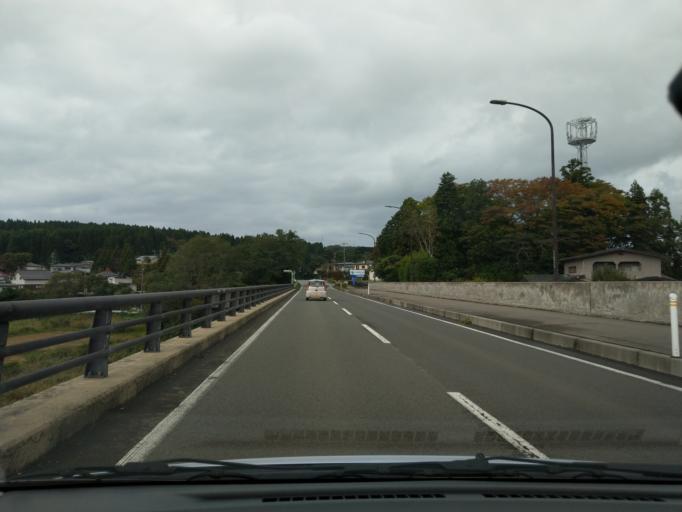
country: JP
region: Akita
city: Akita Shi
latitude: 39.6696
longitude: 140.0857
